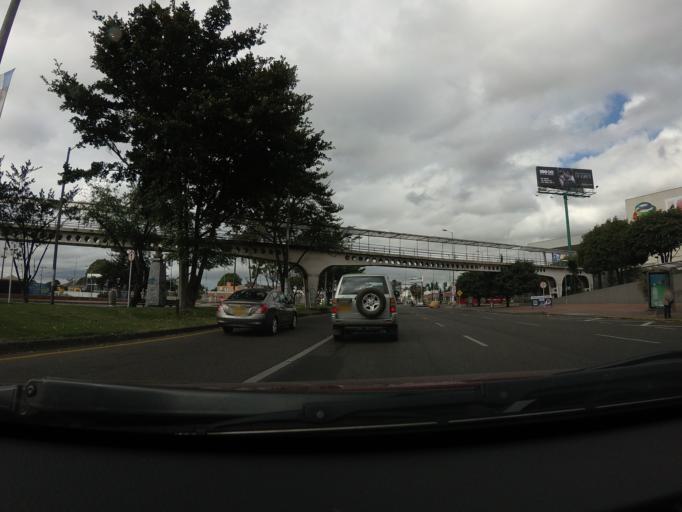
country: CO
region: Bogota D.C.
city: Barrio San Luis
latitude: 4.7113
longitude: -74.0710
